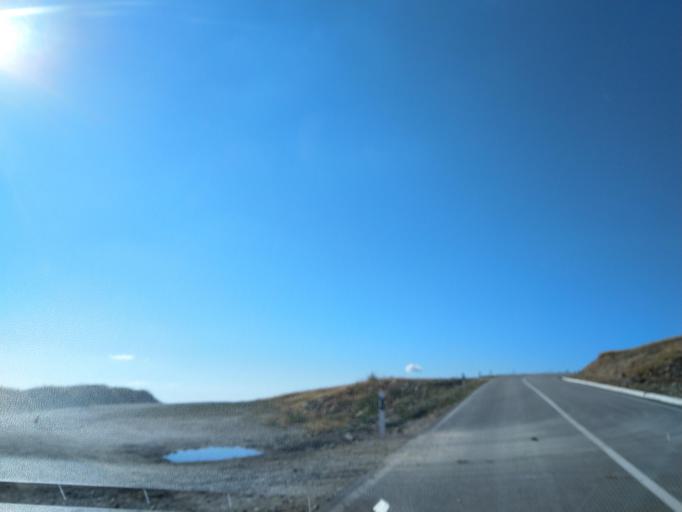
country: RS
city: Sokolovica
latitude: 43.3260
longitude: 20.2841
